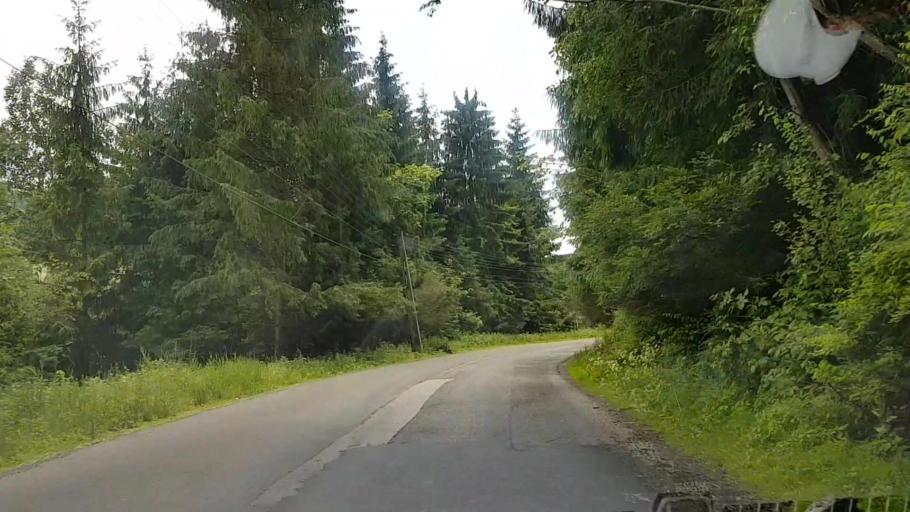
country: RO
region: Suceava
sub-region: Comuna Crucea
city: Crucea
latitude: 47.3495
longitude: 25.6054
